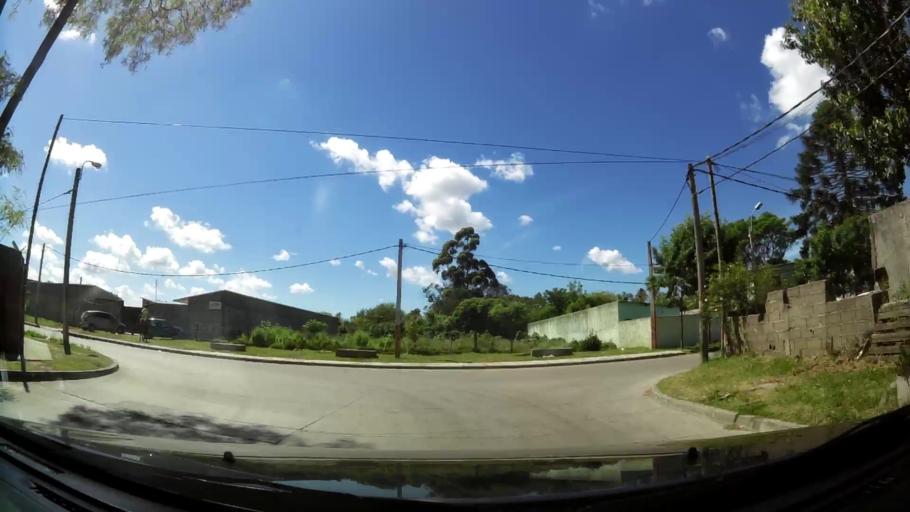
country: UY
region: Montevideo
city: Montevideo
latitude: -34.8444
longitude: -56.1398
